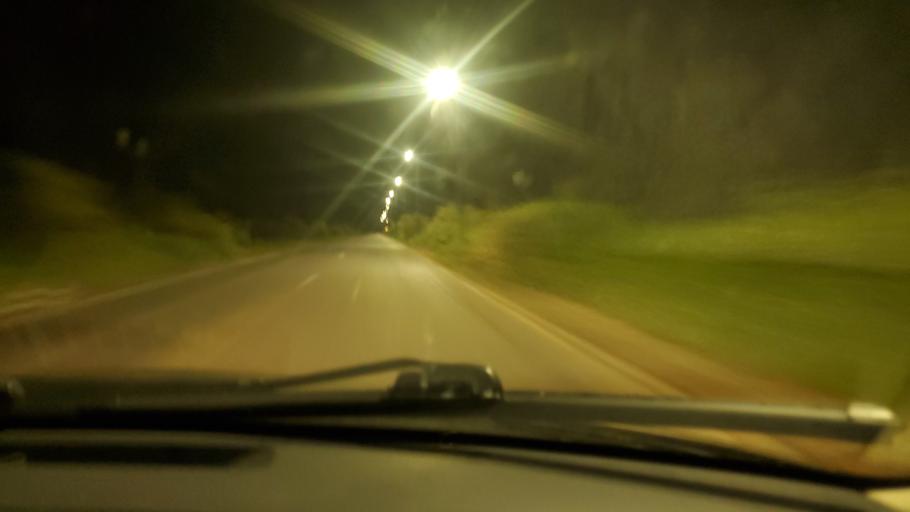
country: SN
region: Thies
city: Thies Nones
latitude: 14.8186
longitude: -16.9491
